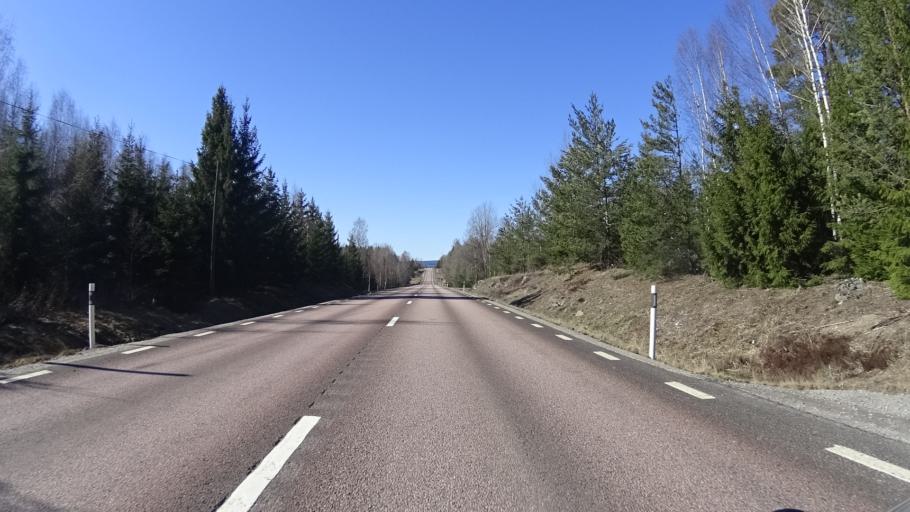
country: SE
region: Vaermland
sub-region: Sunne Kommun
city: Sunne
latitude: 59.6177
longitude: 12.9764
